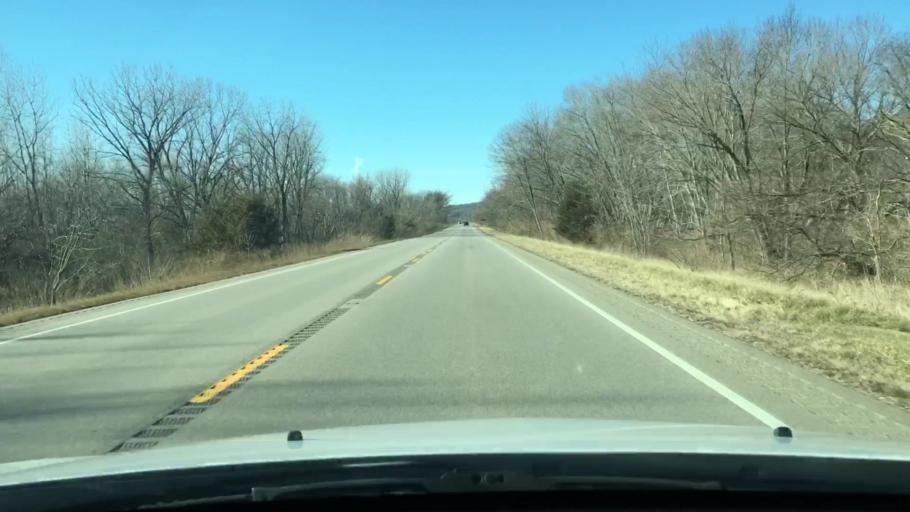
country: US
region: Illinois
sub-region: Peoria County
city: Glasford
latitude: 40.5508
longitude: -89.8250
